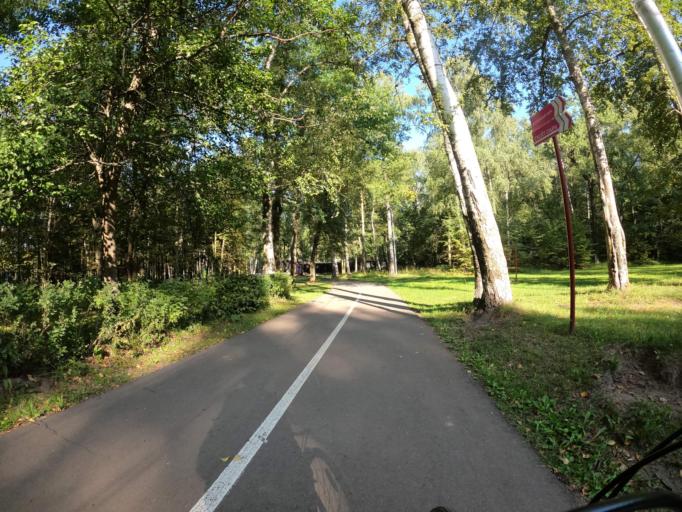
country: RU
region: Moskovskaya
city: Stupino
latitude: 54.8808
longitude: 38.0875
